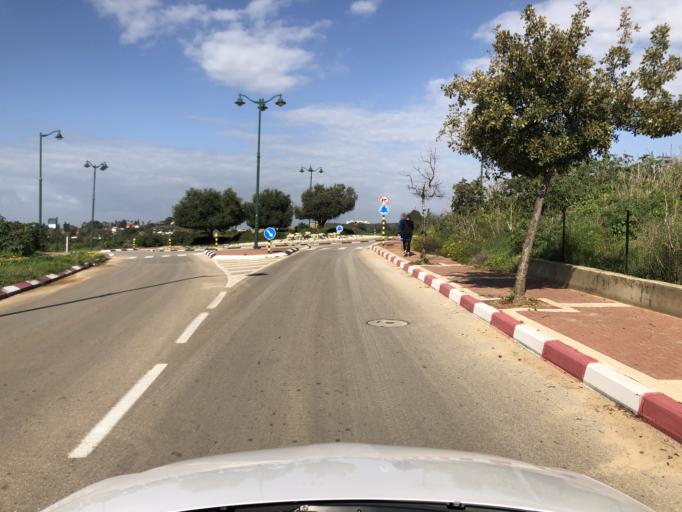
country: IL
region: Central District
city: Ness Ziona
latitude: 31.9146
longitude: 34.7828
